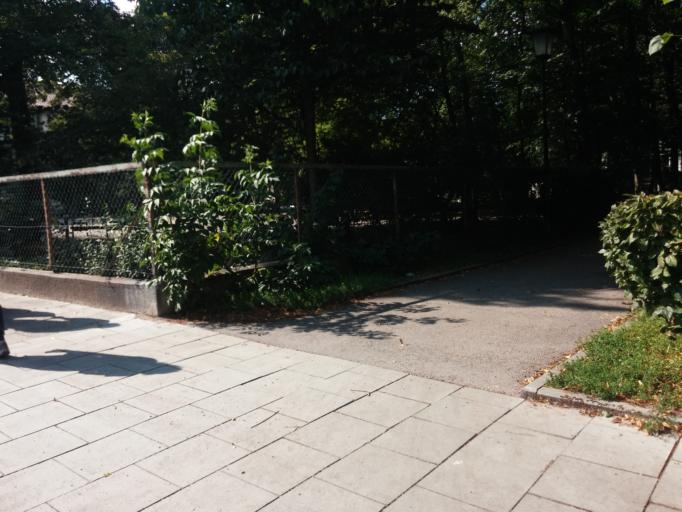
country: DE
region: Bavaria
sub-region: Upper Bavaria
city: Munich
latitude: 48.1642
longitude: 11.5678
